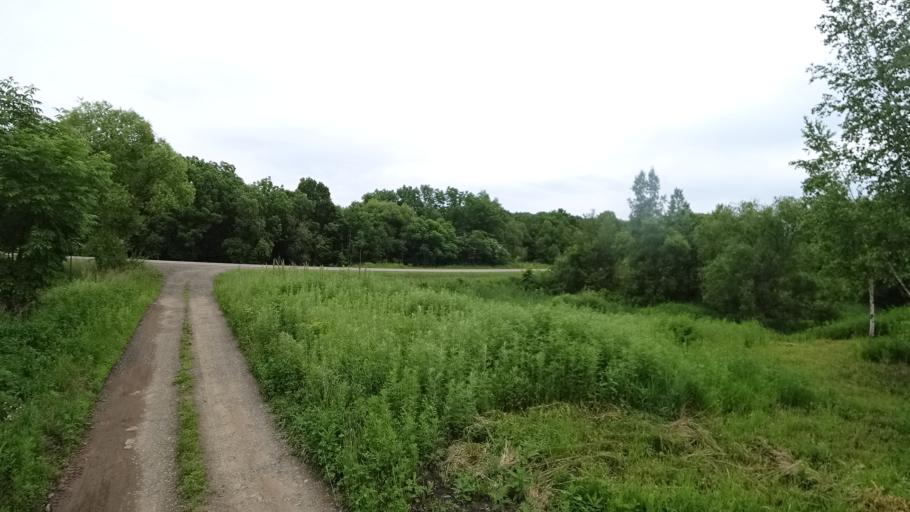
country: RU
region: Primorskiy
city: Novosysoyevka
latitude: 44.1786
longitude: 133.3473
